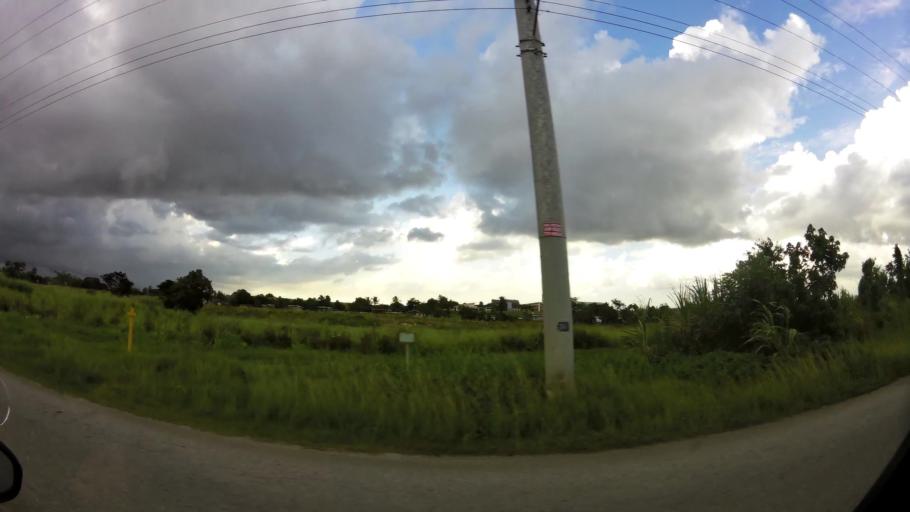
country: TT
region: City of San Fernando
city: Mon Repos
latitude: 10.2622
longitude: -61.4336
